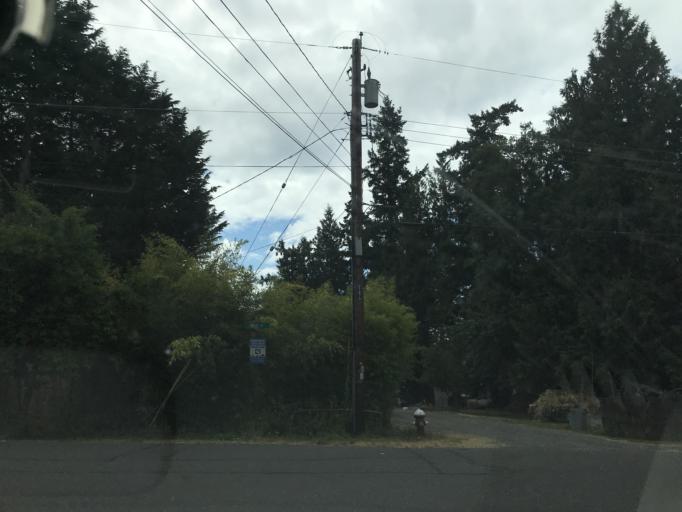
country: US
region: Washington
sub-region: Whatcom County
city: Bellingham
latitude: 48.7211
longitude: -122.4826
